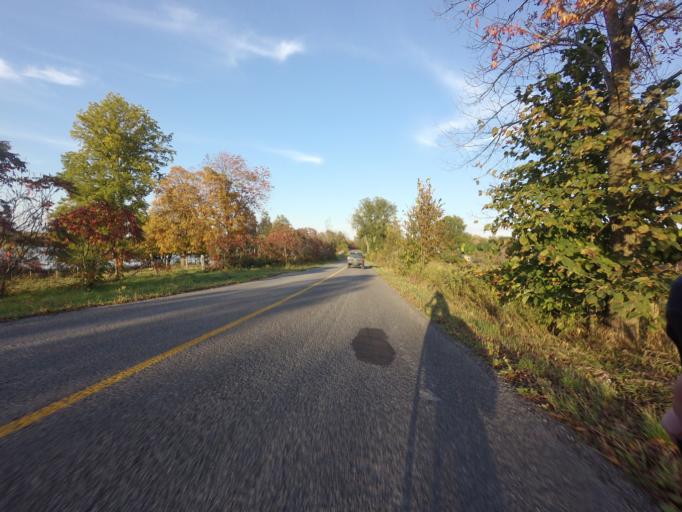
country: CA
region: Ontario
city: Gananoque
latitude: 44.3872
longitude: -76.3301
